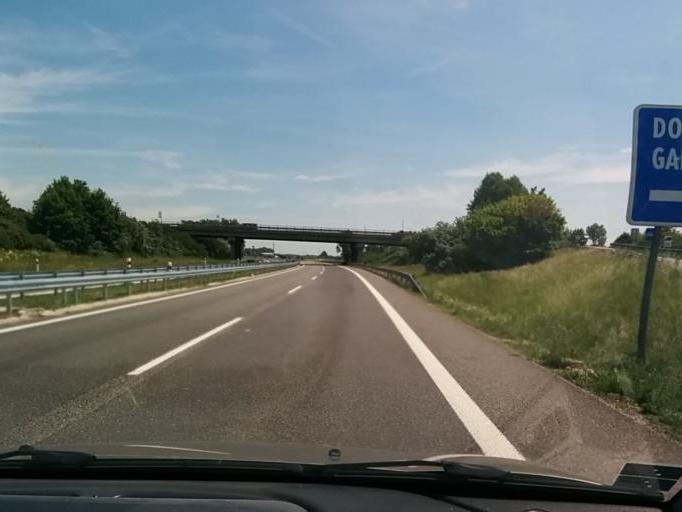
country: SK
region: Trnavsky
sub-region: Okres Galanta
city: Galanta
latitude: 48.2587
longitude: 17.7431
